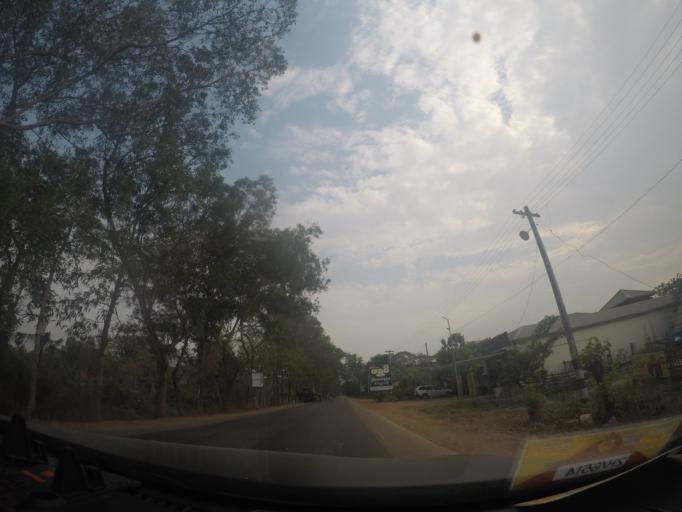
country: MM
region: Bago
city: Paungde
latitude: 18.2489
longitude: 95.6445
